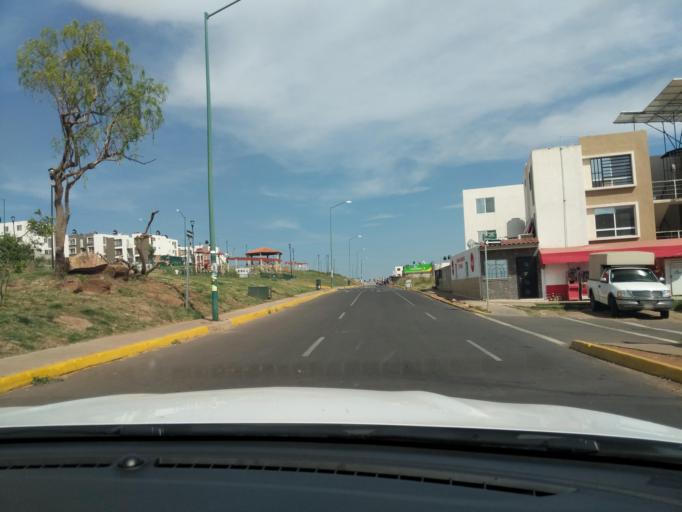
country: MX
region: Jalisco
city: San Jose del Castillo
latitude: 20.5208
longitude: -103.2229
